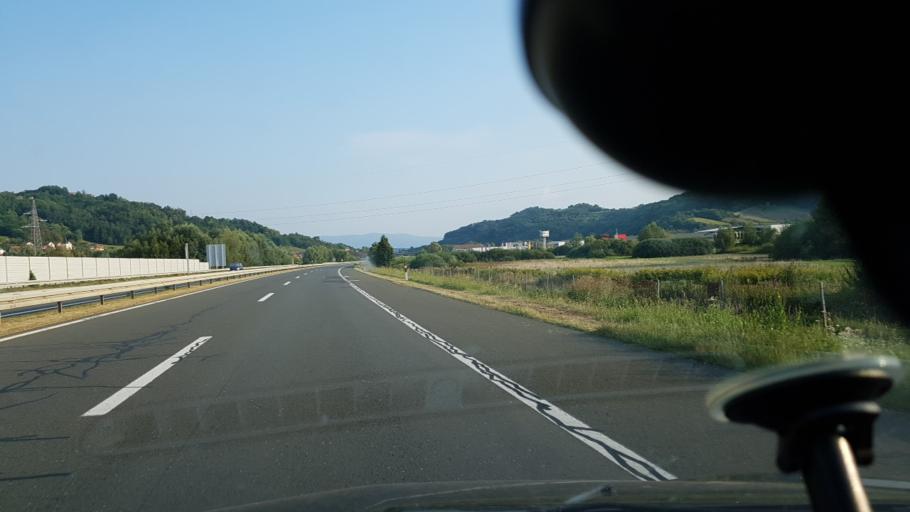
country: HR
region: Krapinsko-Zagorska
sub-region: Grad Krapina
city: Krapina
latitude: 46.1241
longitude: 15.8902
